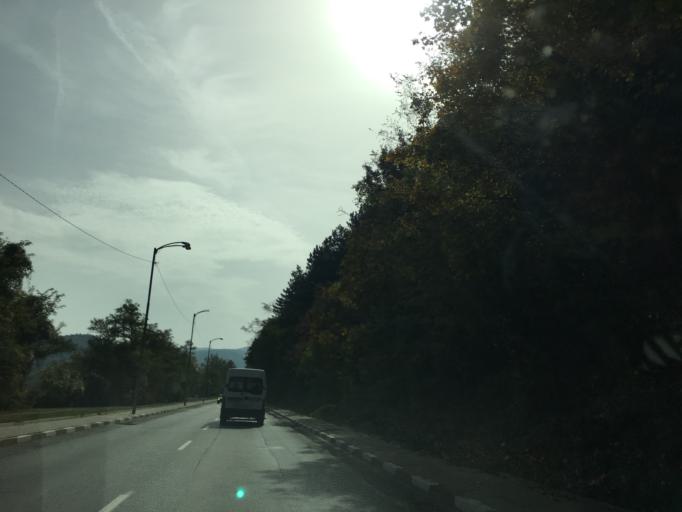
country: BG
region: Sofia-Capital
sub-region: Stolichna Obshtina
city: Sofia
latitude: 42.5916
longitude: 23.4178
